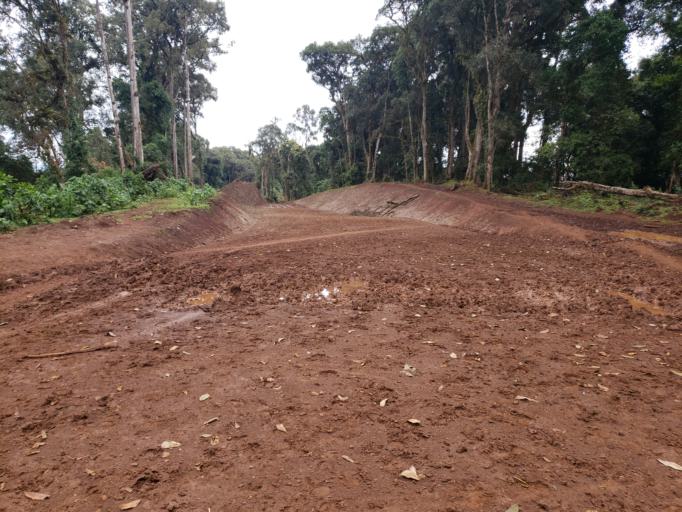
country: ET
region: Oromiya
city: Dodola
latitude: 6.5867
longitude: 39.4131
